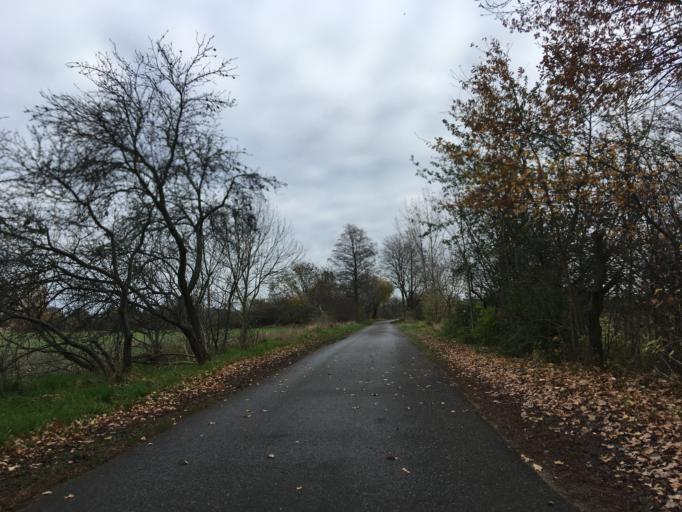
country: DE
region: Brandenburg
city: Drehnow
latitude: 51.8605
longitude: 14.3878
